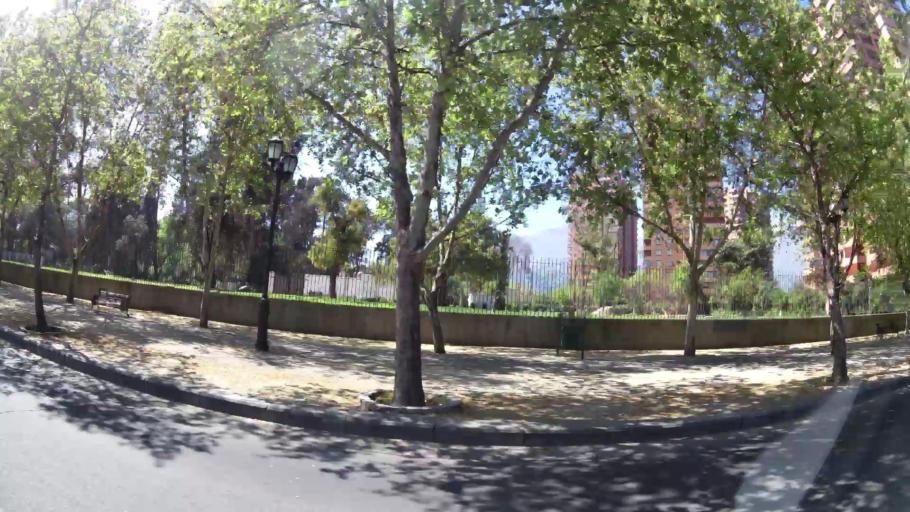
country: CL
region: Santiago Metropolitan
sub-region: Provincia de Santiago
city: Villa Presidente Frei, Nunoa, Santiago, Chile
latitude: -33.4197
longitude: -70.5404
